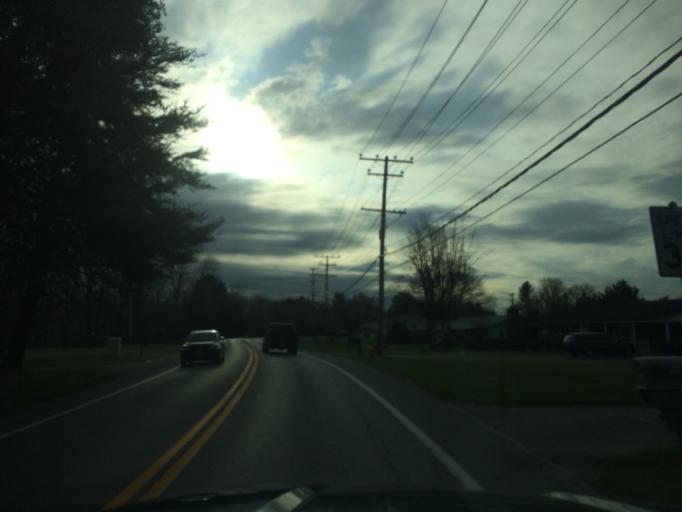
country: US
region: Maryland
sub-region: Howard County
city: North Laurel
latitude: 39.1536
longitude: -76.8782
